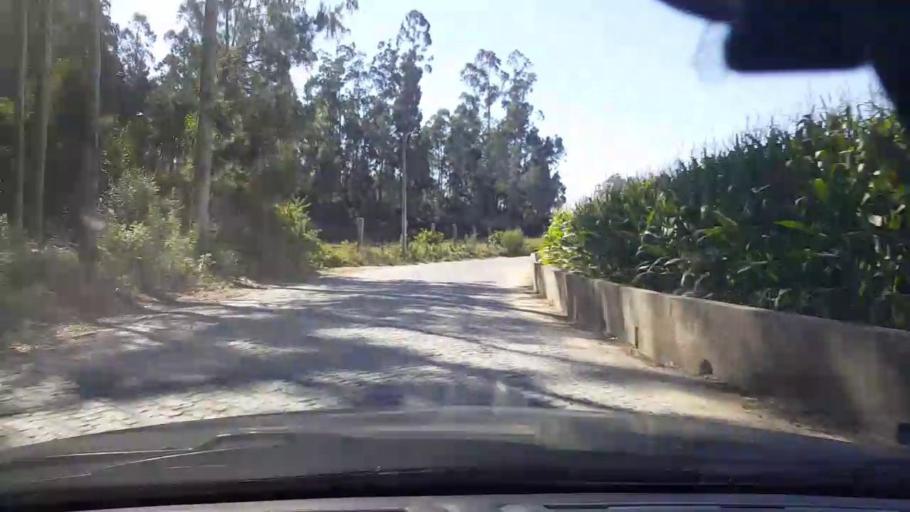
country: PT
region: Porto
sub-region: Maia
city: Gemunde
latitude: 41.2936
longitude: -8.6662
